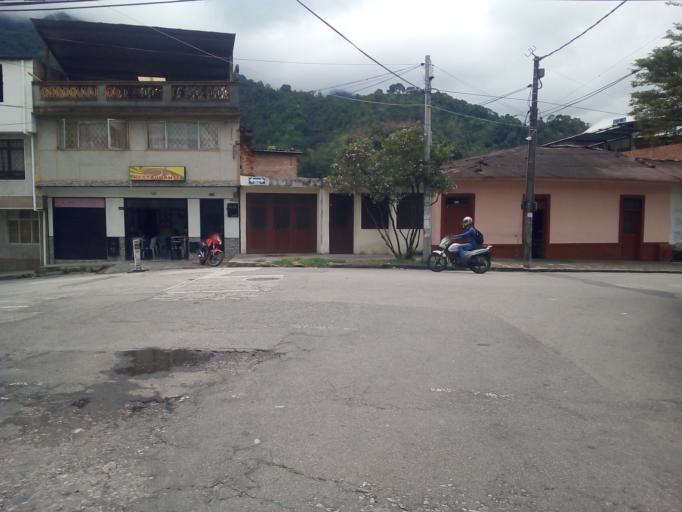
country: CO
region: Tolima
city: Ibague
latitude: 4.4514
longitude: -75.2432
